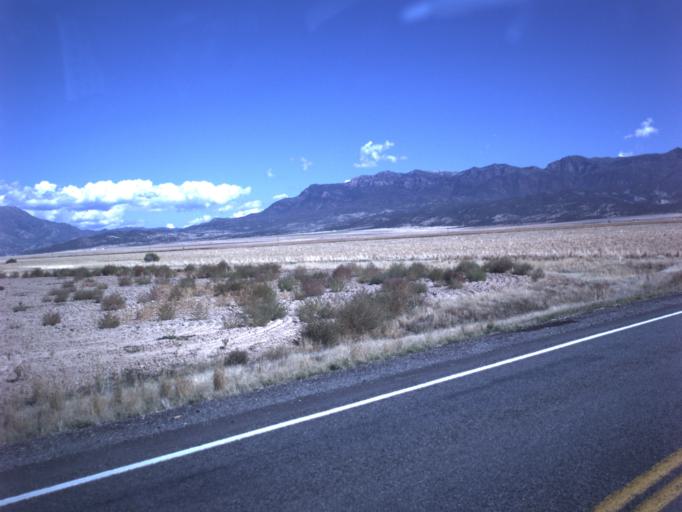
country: US
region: Utah
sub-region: Juab County
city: Nephi
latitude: 39.5577
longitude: -111.9158
